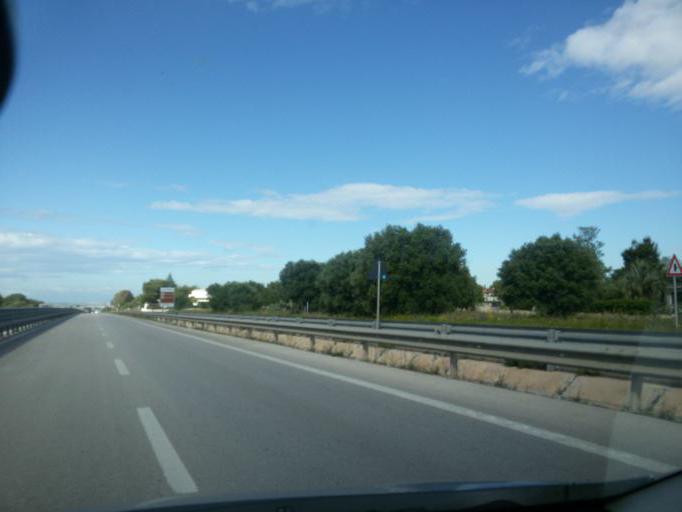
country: IT
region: Apulia
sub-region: Provincia di Taranto
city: Grottaglie
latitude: 40.5326
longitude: 17.4553
